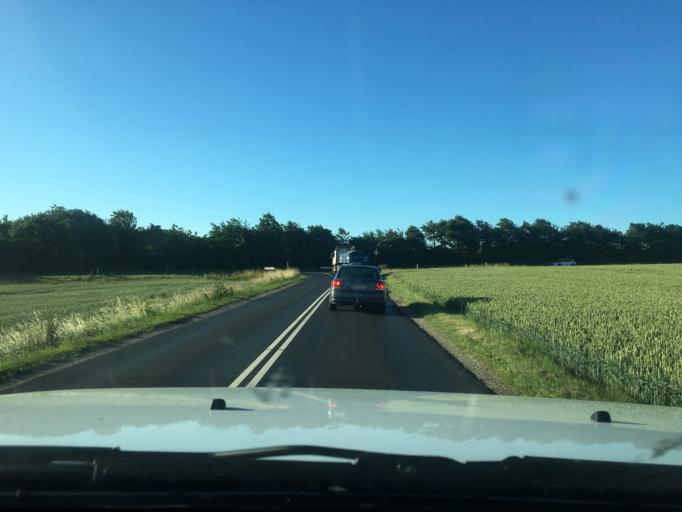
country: DK
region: Central Jutland
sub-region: Randers Kommune
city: Langa
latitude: 56.3886
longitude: 9.9645
